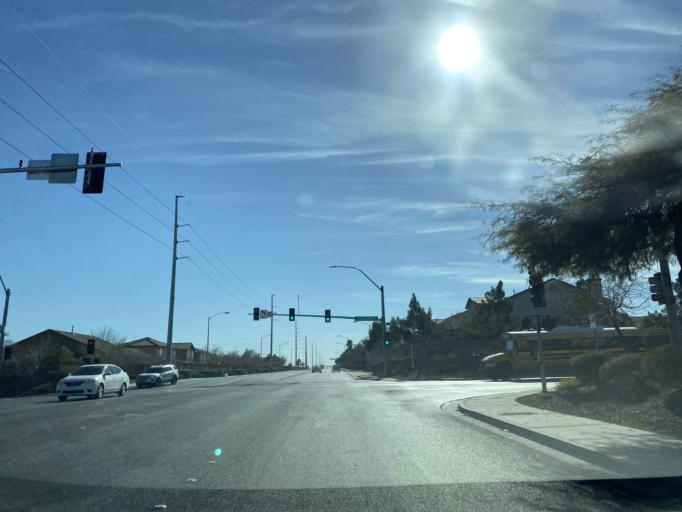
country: US
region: Nevada
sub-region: Clark County
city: North Las Vegas
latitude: 36.2324
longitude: -115.1435
